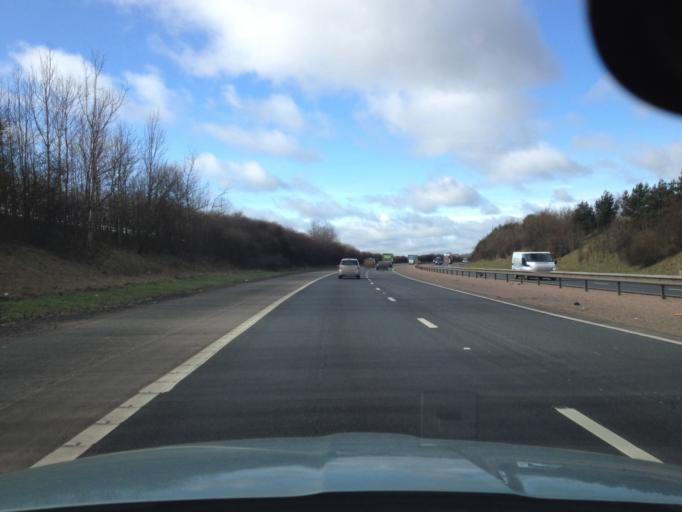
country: GB
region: Scotland
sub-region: Edinburgh
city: Currie
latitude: 55.9191
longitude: -3.3272
